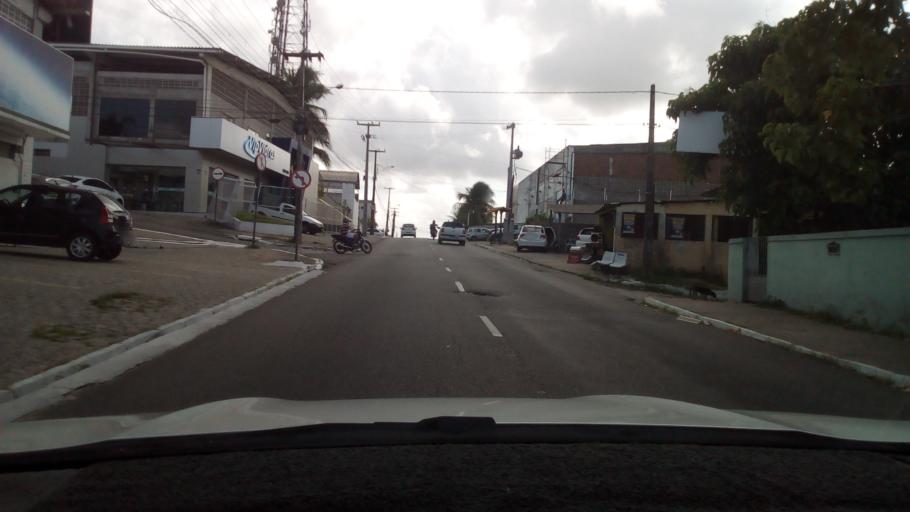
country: BR
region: Paraiba
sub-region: Joao Pessoa
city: Joao Pessoa
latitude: -7.1011
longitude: -34.8632
